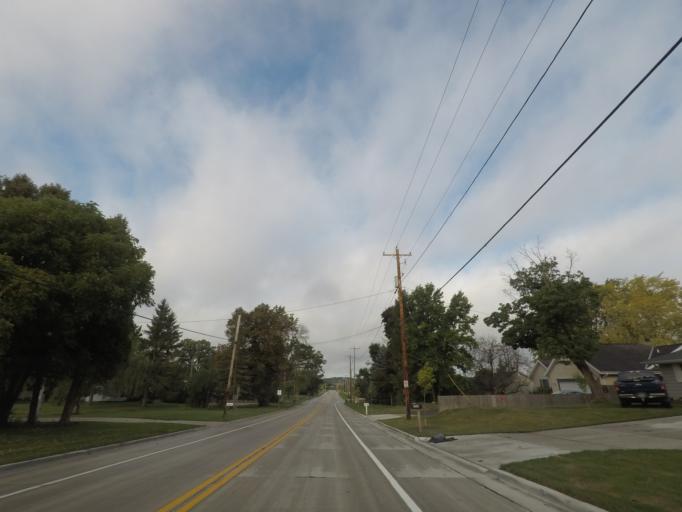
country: US
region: Wisconsin
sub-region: Waukesha County
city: Waukesha
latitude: 43.0321
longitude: -88.2646
